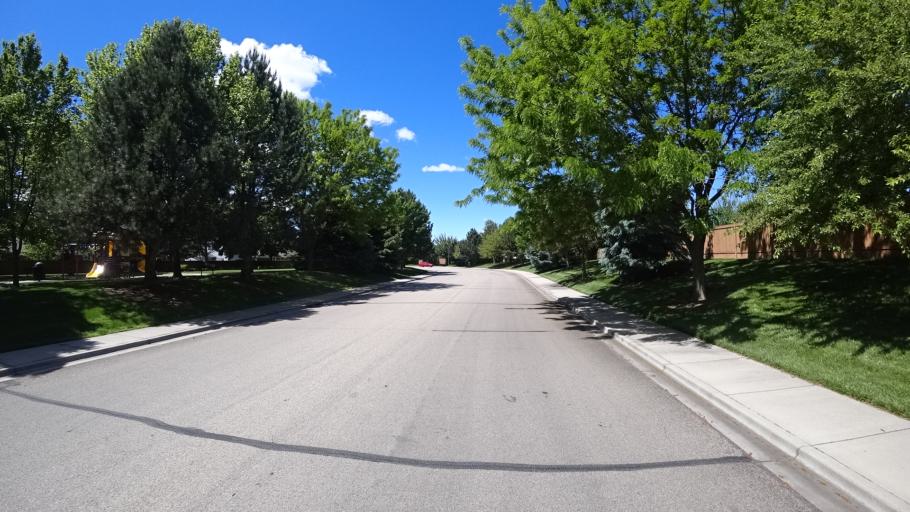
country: US
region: Idaho
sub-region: Ada County
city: Eagle
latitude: 43.6431
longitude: -116.3470
